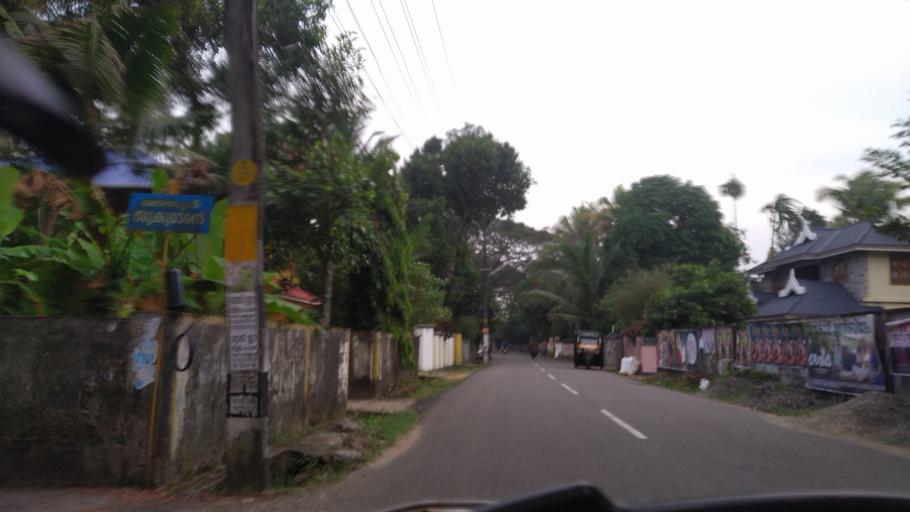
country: IN
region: Kerala
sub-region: Ernakulam
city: Elur
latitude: 10.1419
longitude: 76.2474
